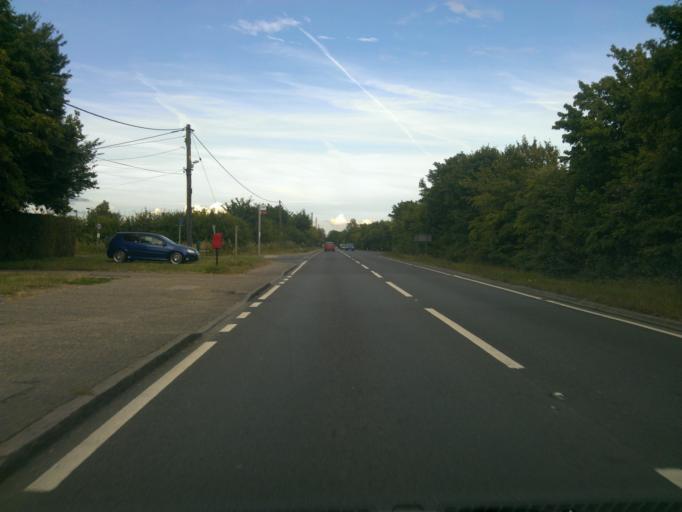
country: GB
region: England
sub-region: Essex
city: Marks Tey
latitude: 51.8764
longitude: 0.7438
